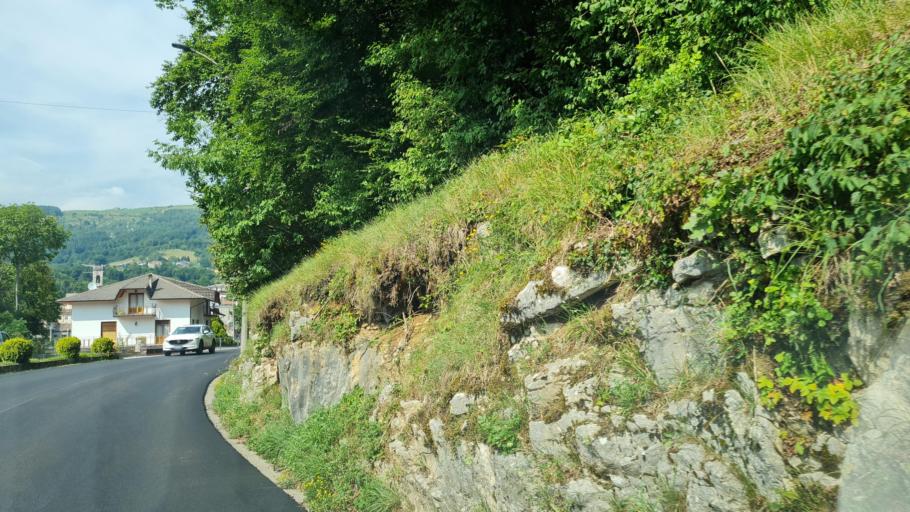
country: IT
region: Veneto
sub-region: Provincia di Vicenza
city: Conco
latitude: 45.7929
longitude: 11.6311
